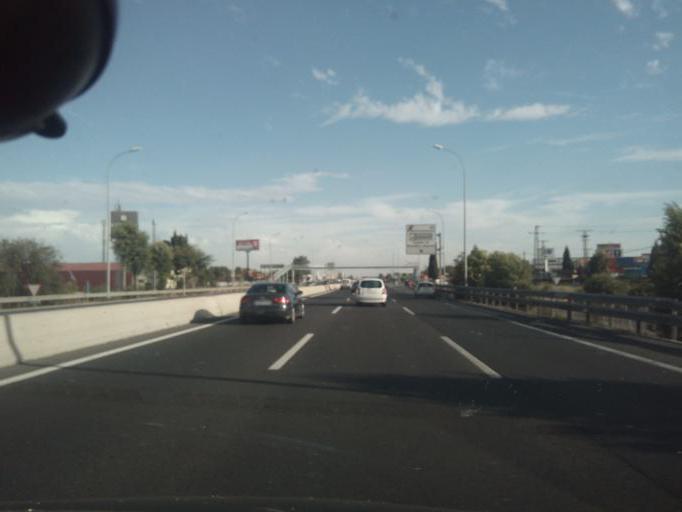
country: ES
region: Madrid
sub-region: Provincia de Madrid
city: Valdemoro
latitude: 40.2126
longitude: -3.6826
